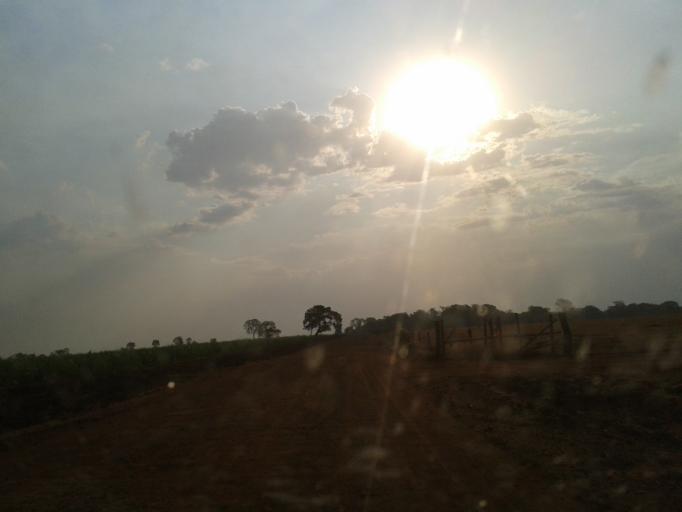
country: BR
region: Minas Gerais
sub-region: Capinopolis
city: Capinopolis
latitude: -18.7561
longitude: -49.7051
